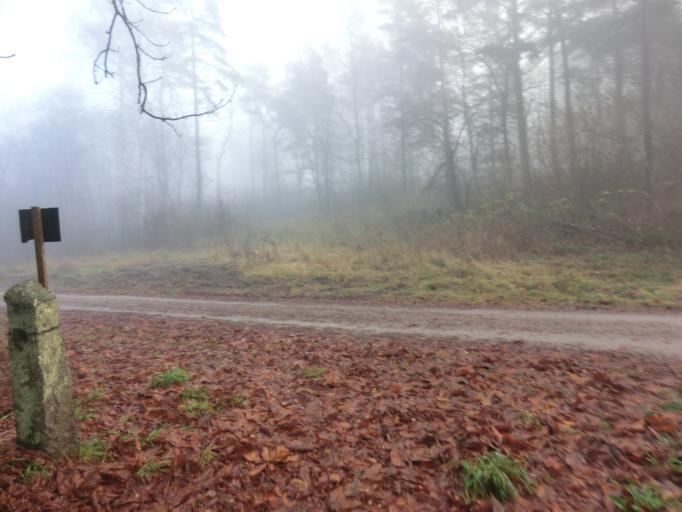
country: SE
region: Skane
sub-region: Lunds Kommun
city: Veberod
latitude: 55.6932
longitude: 13.4979
